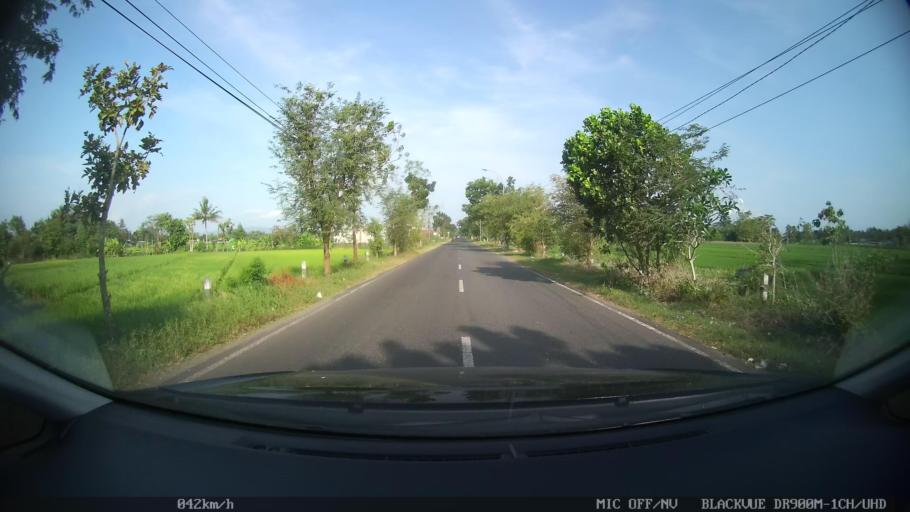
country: ID
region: Daerah Istimewa Yogyakarta
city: Pandak
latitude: -7.9028
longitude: 110.3061
